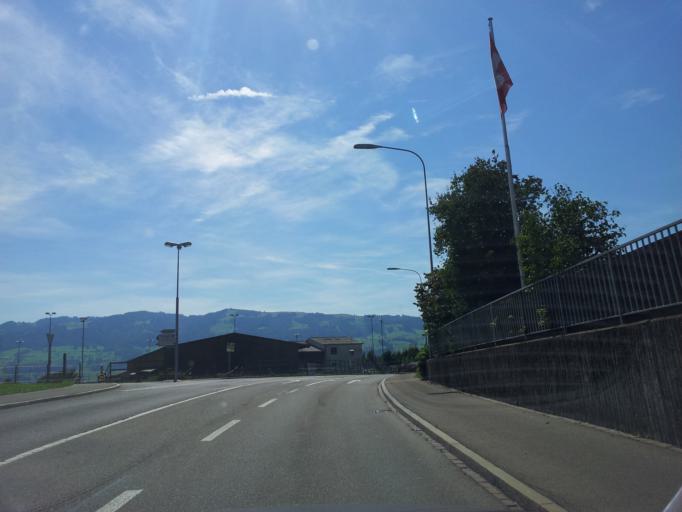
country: CH
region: Saint Gallen
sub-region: Wahlkreis See-Gaster
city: Jona
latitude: 47.2229
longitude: 8.8429
